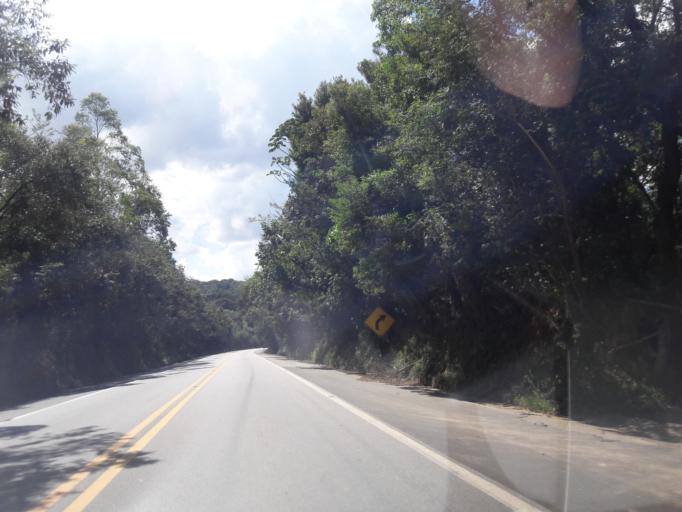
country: BR
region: Sao Paulo
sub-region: Campo Limpo Paulista
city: Campo Limpo Paulista
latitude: -23.2446
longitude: -46.7916
